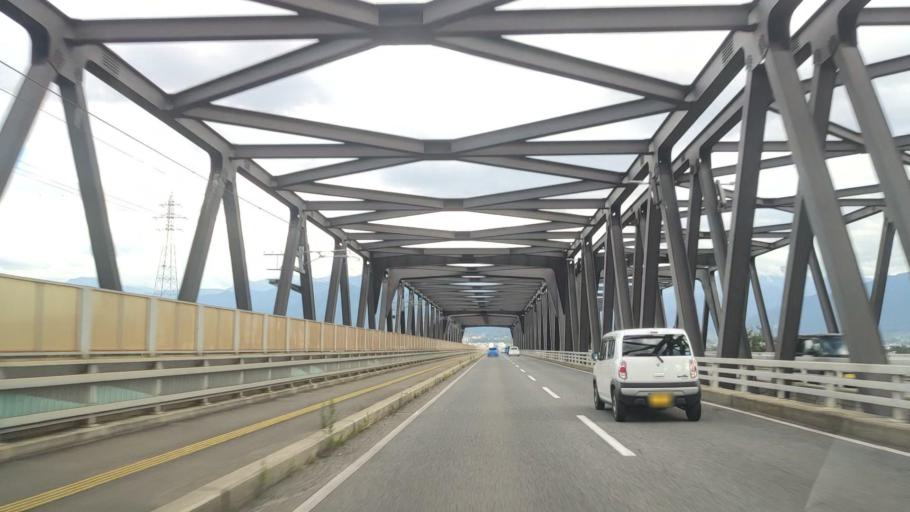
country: JP
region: Nagano
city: Suzaka
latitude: 36.6633
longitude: 138.2686
